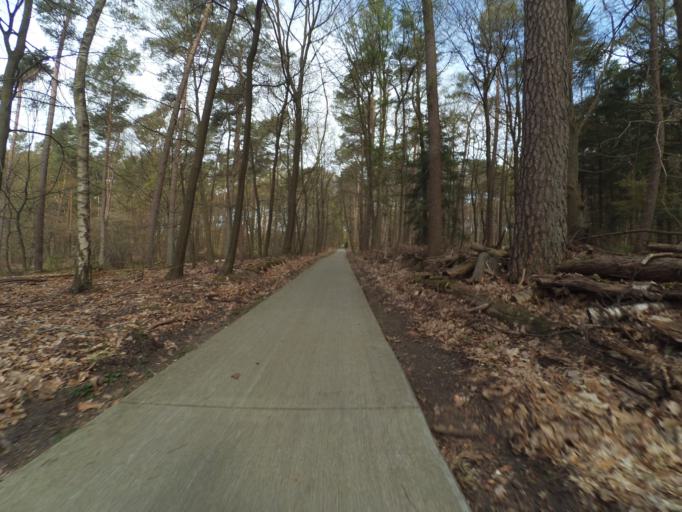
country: NL
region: Gelderland
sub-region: Gemeente Nunspeet
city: Nunspeet
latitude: 52.3454
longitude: 5.8069
